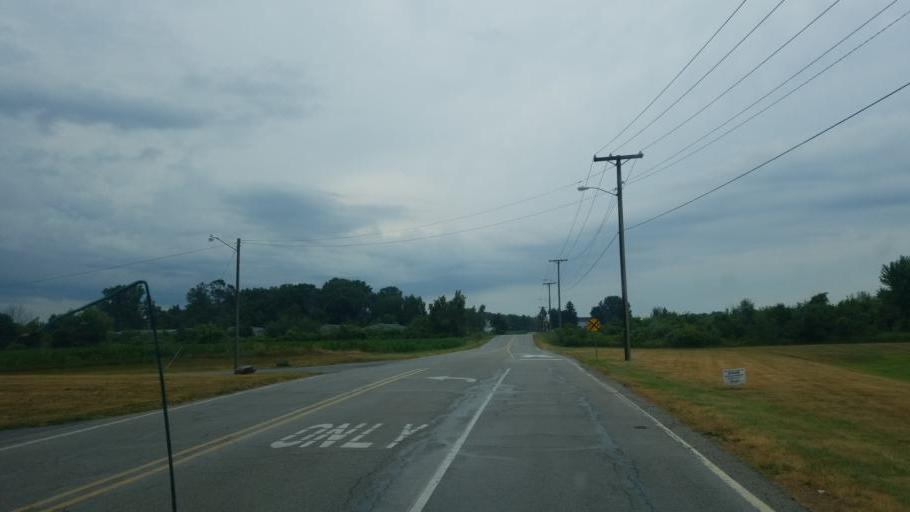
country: US
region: Indiana
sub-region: Steuben County
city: Hamilton
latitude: 41.5310
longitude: -84.9317
